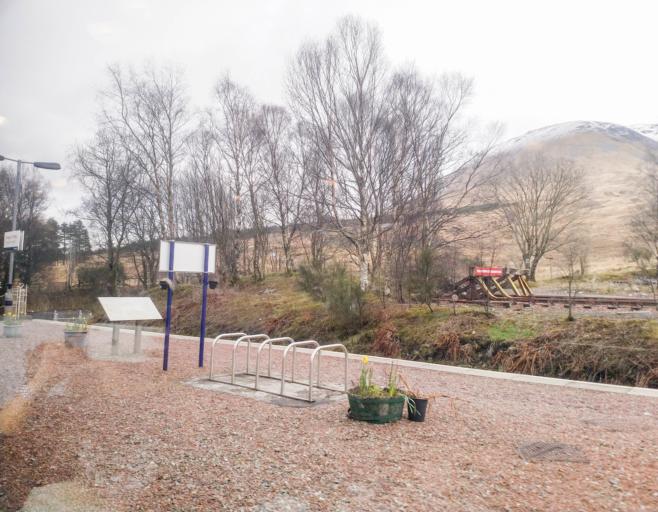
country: GB
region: Scotland
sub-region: Highland
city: Spean Bridge
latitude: 56.5165
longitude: -4.7643
